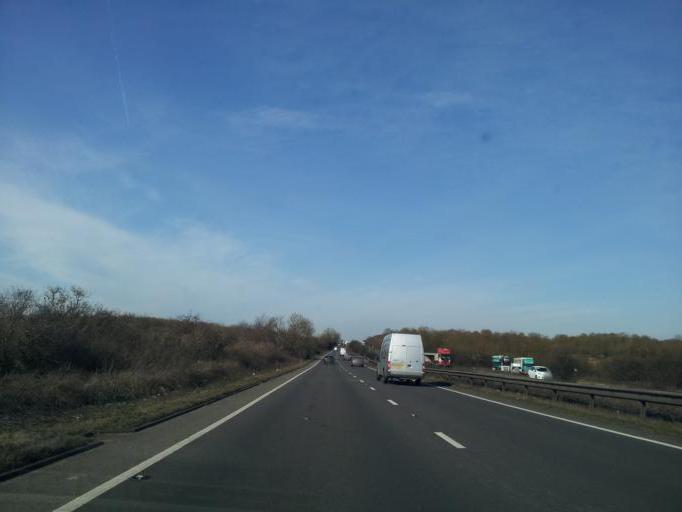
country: GB
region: England
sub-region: District of Rutland
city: Clipsham
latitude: 52.7130
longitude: -0.5928
